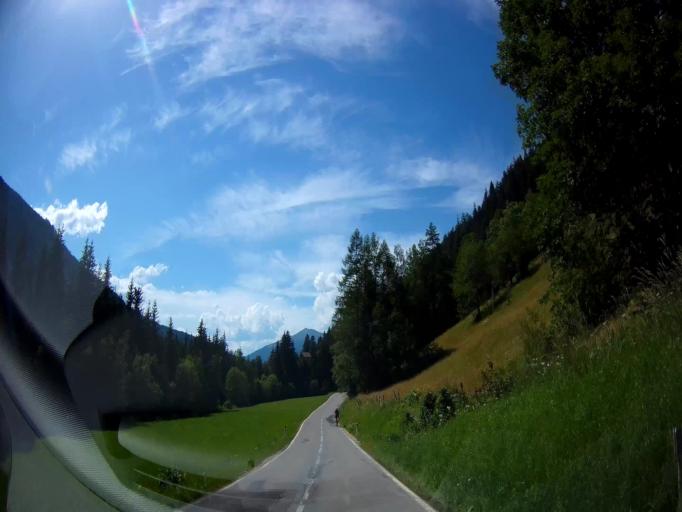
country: AT
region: Salzburg
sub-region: Politischer Bezirk Tamsweg
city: Thomatal
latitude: 47.0683
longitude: 13.7578
